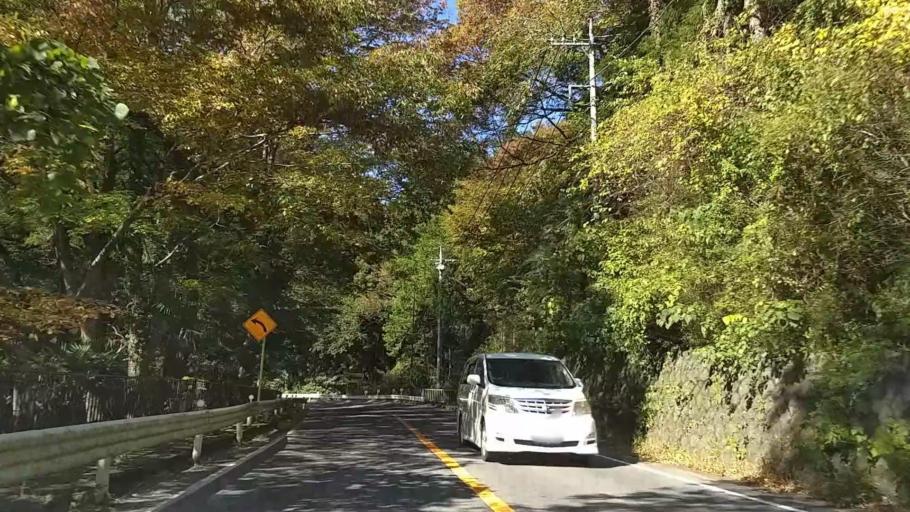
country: JP
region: Yamanashi
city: Uenohara
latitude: 35.6190
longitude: 139.1335
